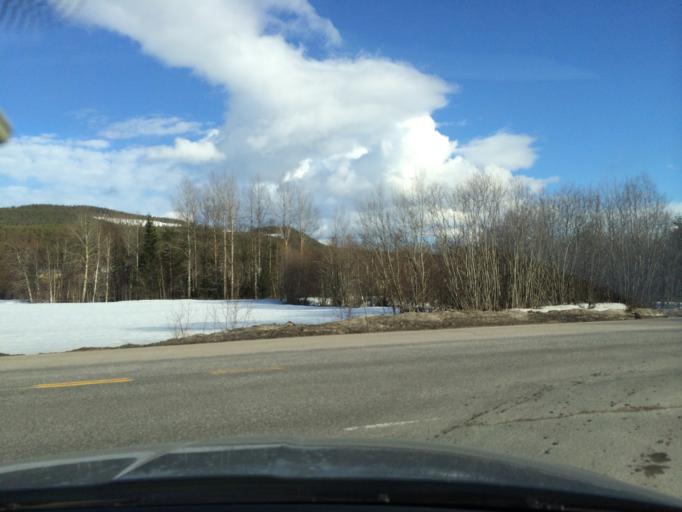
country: NO
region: Hedmark
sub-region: Trysil
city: Innbygda
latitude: 61.3415
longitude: 12.2202
